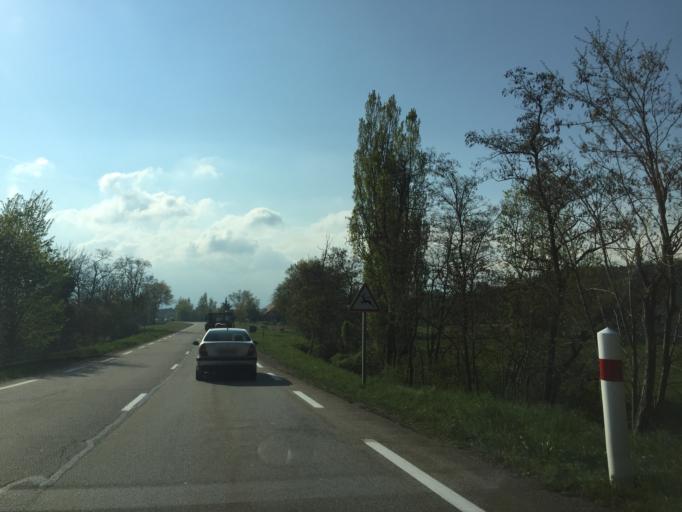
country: FR
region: Rhone-Alpes
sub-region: Departement de l'Isere
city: La Motte-Saint-Martin
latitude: 44.8550
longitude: 5.6145
